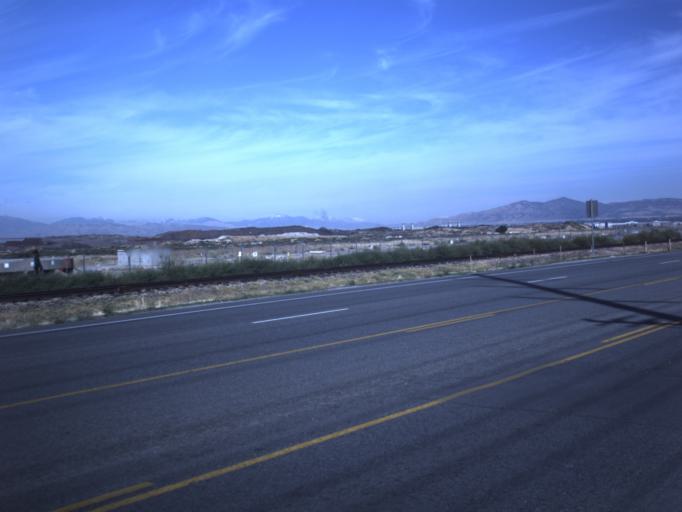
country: US
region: Utah
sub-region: Utah County
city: Lindon
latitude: 40.3133
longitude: -111.7349
